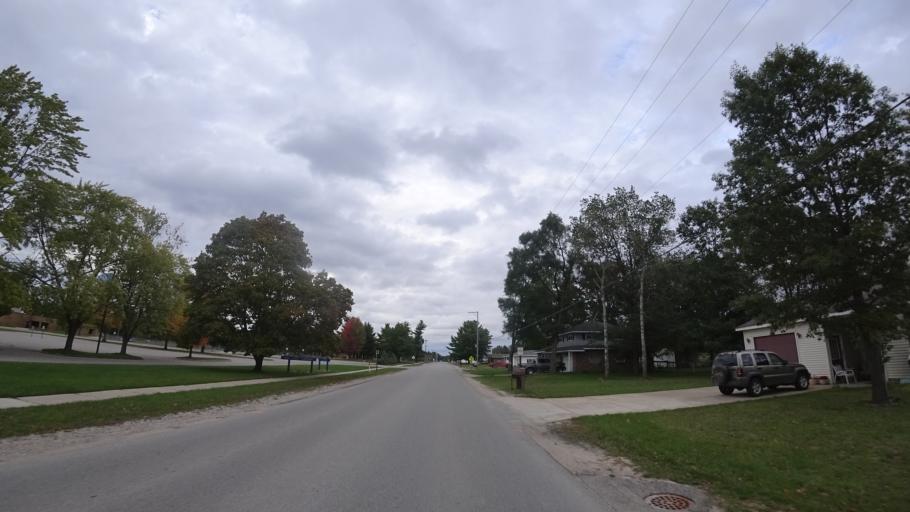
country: US
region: Michigan
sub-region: Kalkaska County
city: Kalkaska
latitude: 44.7374
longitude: -85.1846
